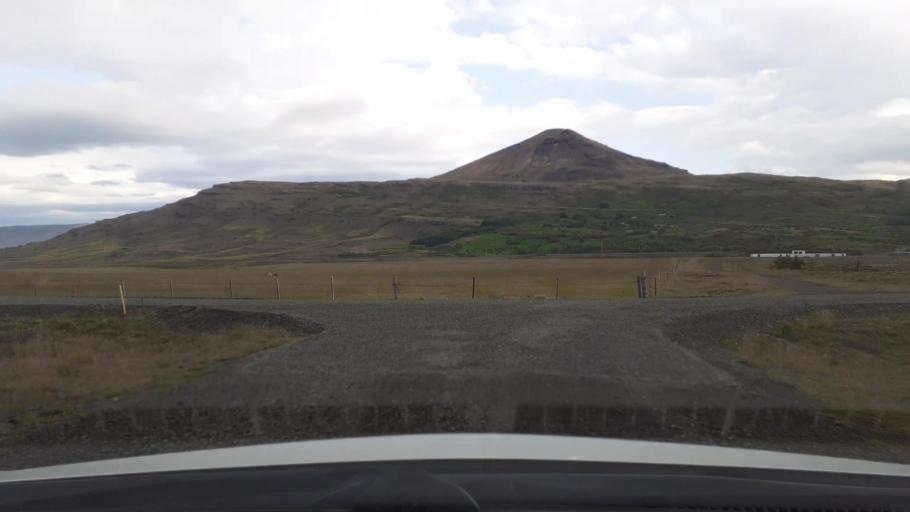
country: IS
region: Capital Region
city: Mosfellsbaer
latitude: 64.2908
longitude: -21.4613
